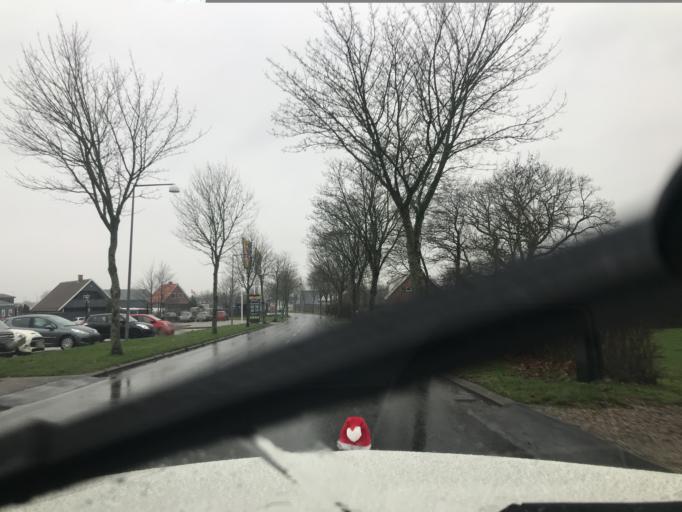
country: DK
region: South Denmark
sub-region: Aabenraa Kommune
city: Rodekro
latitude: 55.0693
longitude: 9.3604
